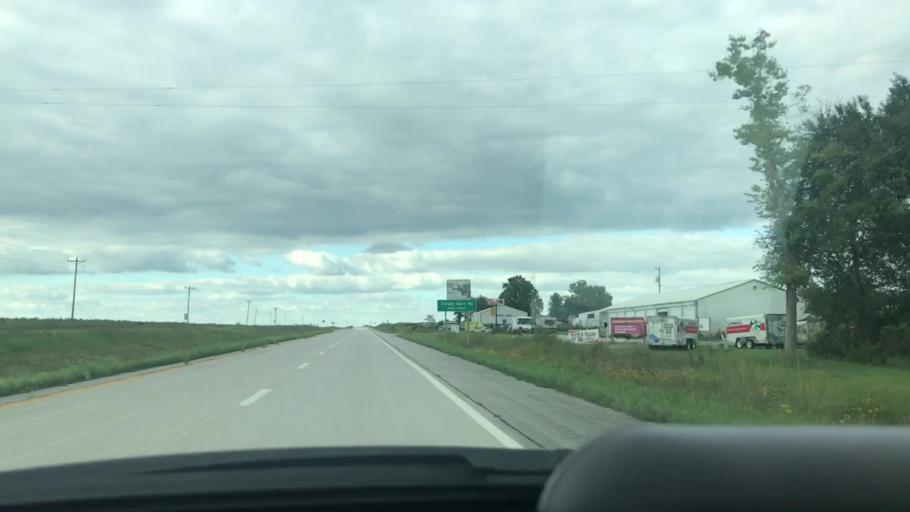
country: US
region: Missouri
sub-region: Benton County
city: Lincoln
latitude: 38.3516
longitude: -93.3393
